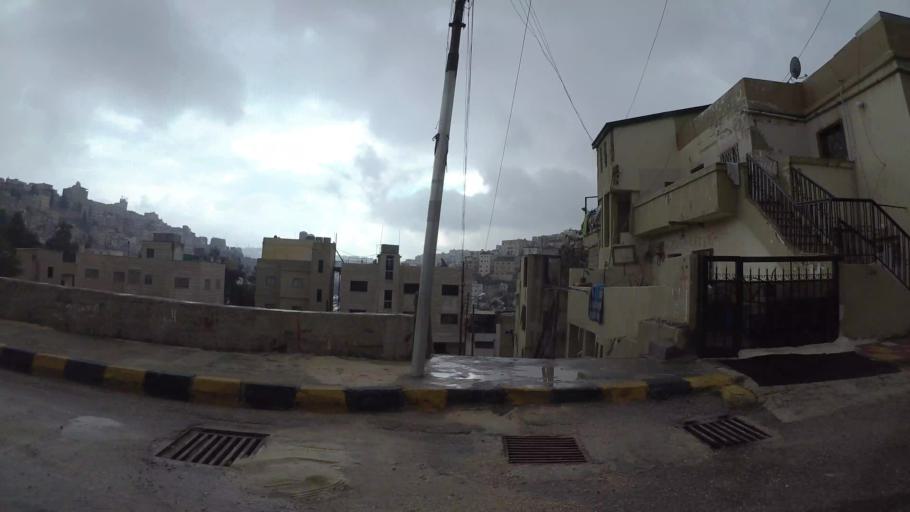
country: JO
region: Amman
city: Amman
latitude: 31.9491
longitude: 35.9119
